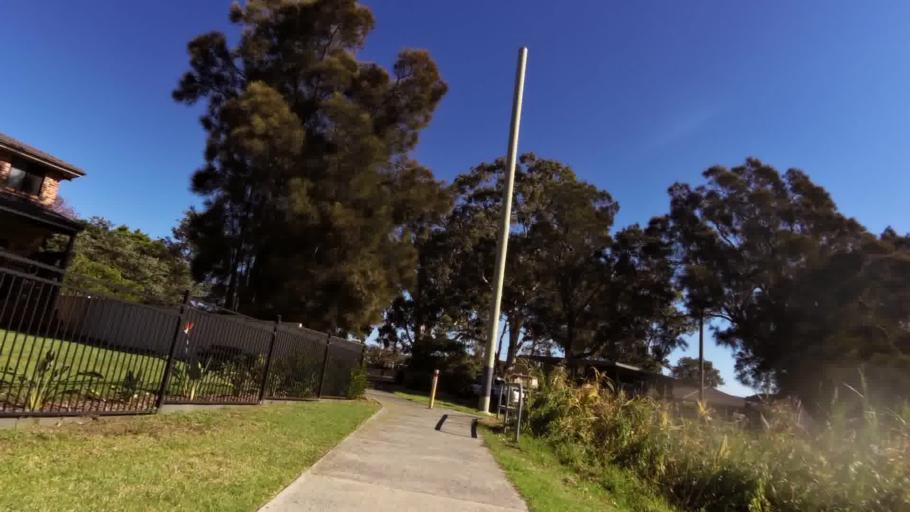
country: AU
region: New South Wales
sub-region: Shellharbour
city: Albion Park Rail
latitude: -34.5553
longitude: 150.8187
